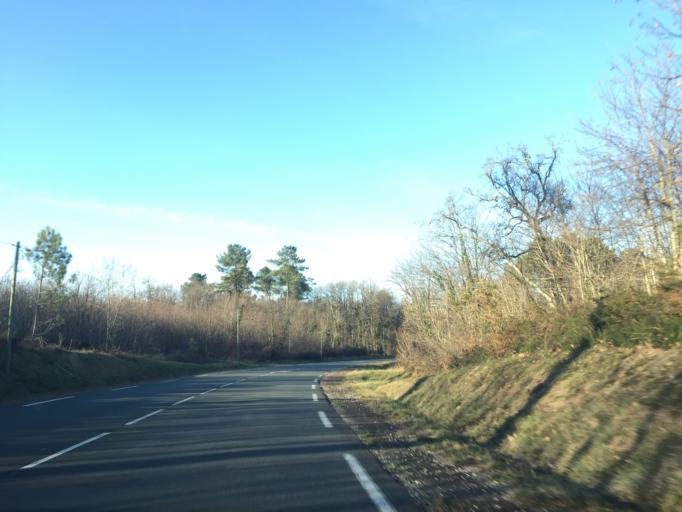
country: FR
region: Aquitaine
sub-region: Departement de la Dordogne
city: Riberac
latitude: 45.1876
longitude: 0.3761
